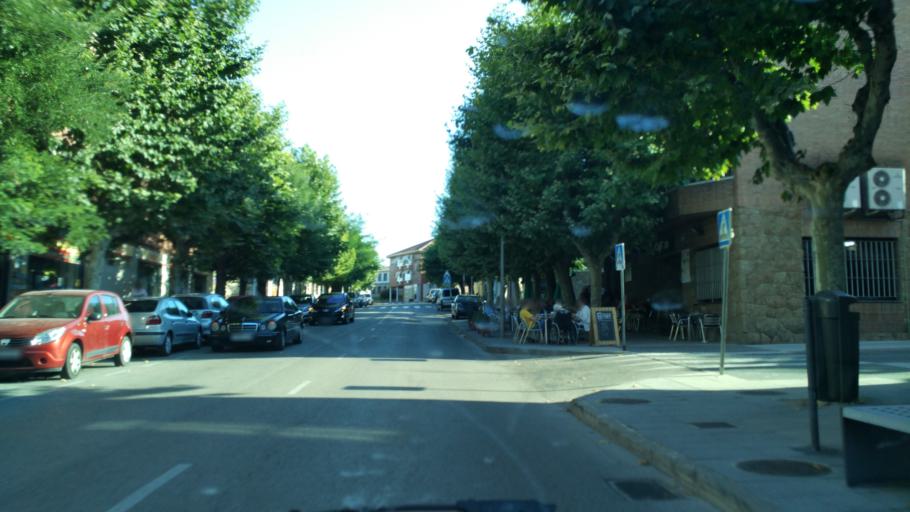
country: ES
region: Madrid
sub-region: Provincia de Madrid
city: San Agustin de Guadalix
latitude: 40.6793
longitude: -3.6145
